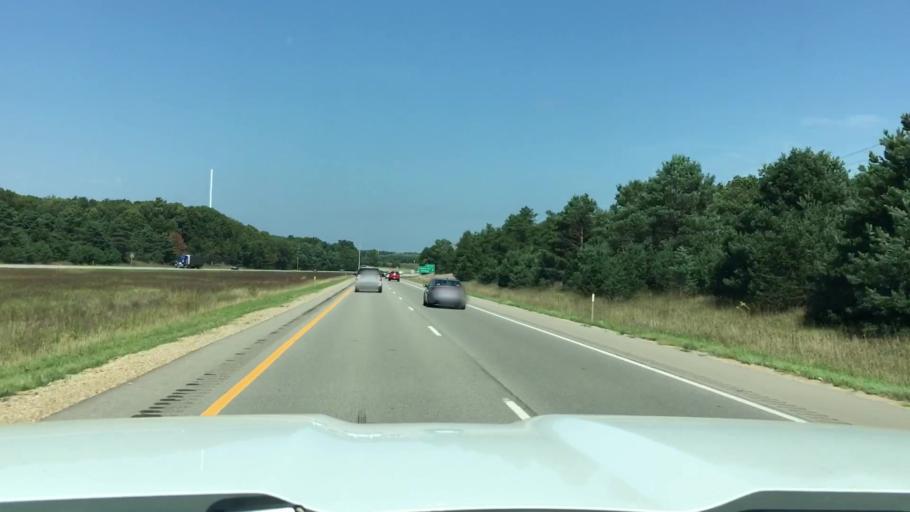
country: US
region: Michigan
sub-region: Kalamazoo County
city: Portage
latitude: 42.1911
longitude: -85.6462
